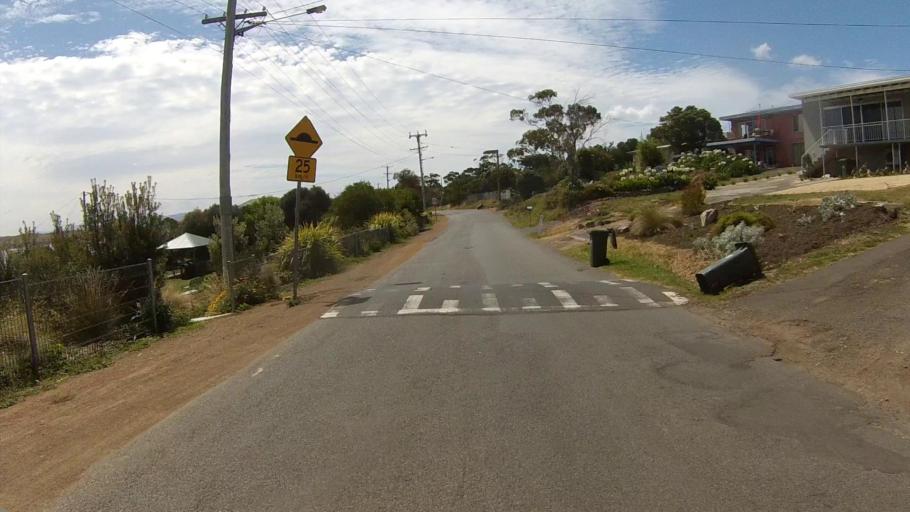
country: AU
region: Tasmania
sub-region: Kingborough
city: Taroona
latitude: -42.9935
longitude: 147.4033
